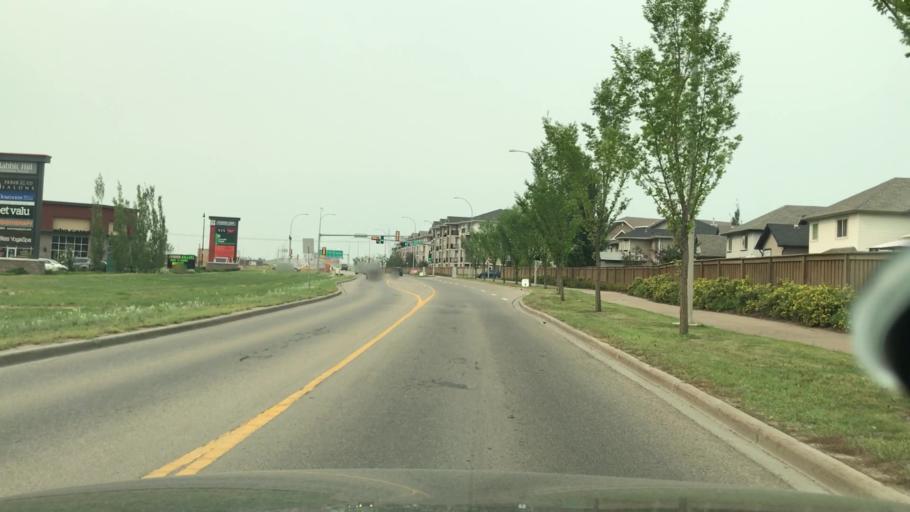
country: CA
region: Alberta
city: Edmonton
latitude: 53.4358
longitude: -113.5732
